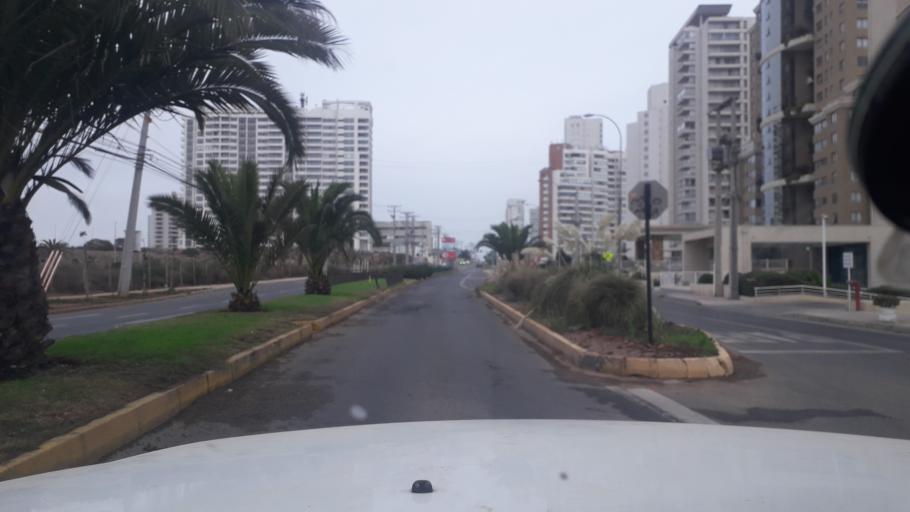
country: CL
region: Valparaiso
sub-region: Provincia de Valparaiso
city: Vina del Mar
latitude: -32.9537
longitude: -71.5439
